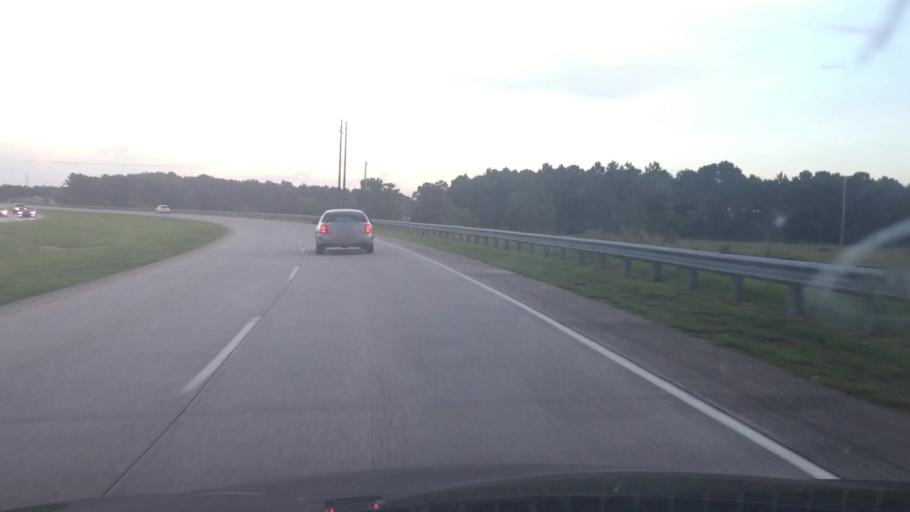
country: US
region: South Carolina
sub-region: Horry County
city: North Myrtle Beach
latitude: 33.8400
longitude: -78.6994
